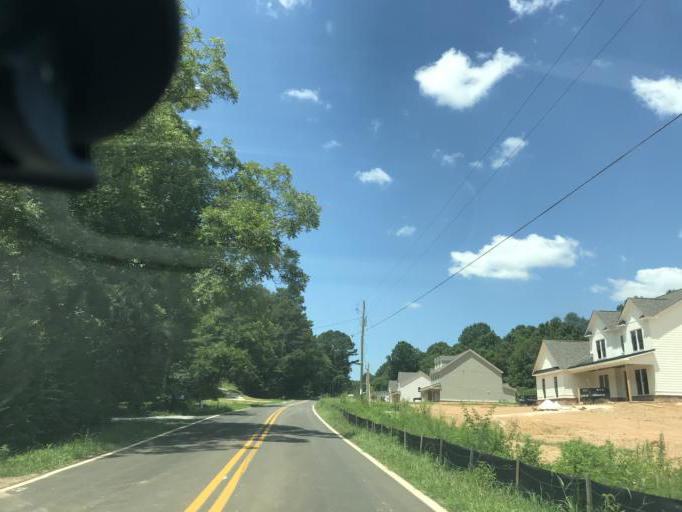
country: US
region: Georgia
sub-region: Forsyth County
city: Cumming
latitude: 34.2686
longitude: -84.2557
